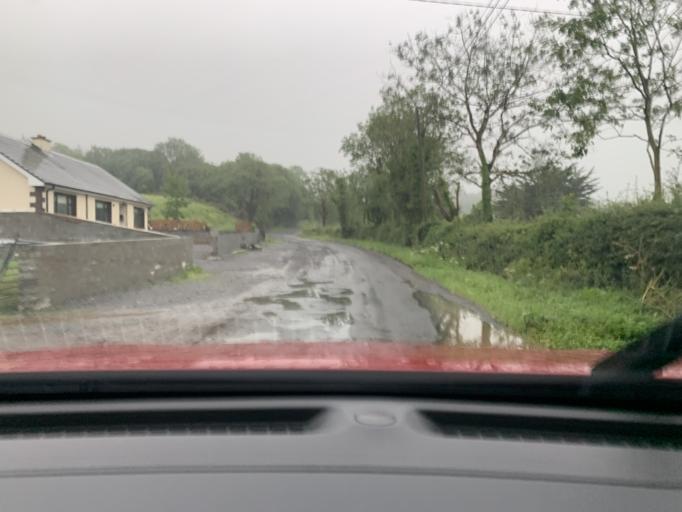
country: IE
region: Connaught
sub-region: Sligo
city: Sligo
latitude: 54.3264
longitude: -8.4227
